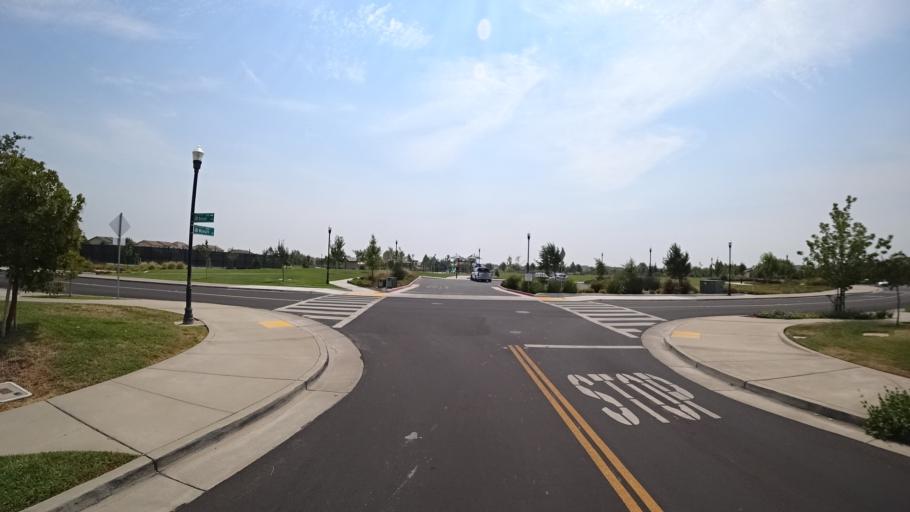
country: US
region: California
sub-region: Sacramento County
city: Laguna
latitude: 38.4022
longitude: -121.4081
